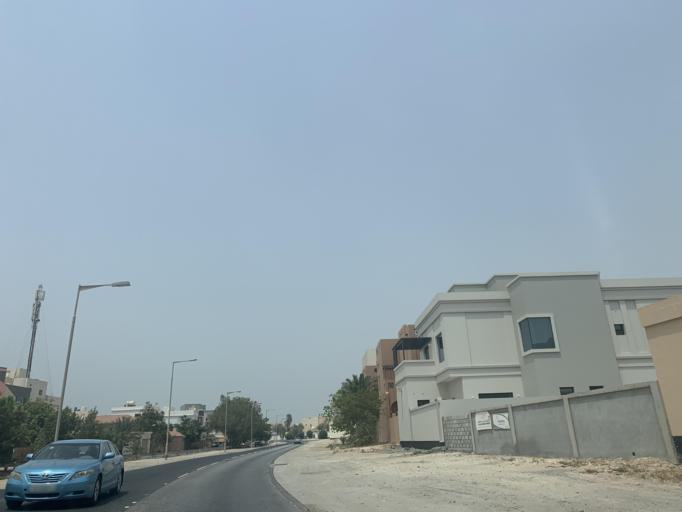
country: BH
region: Northern
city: Madinat `Isa
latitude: 26.1890
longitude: 50.4754
